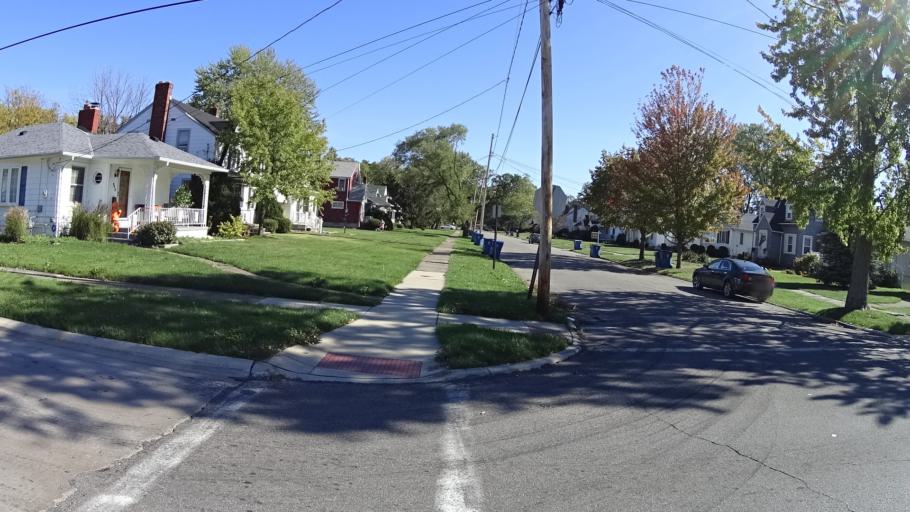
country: US
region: Ohio
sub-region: Lorain County
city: Lorain
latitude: 41.4439
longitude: -82.1793
